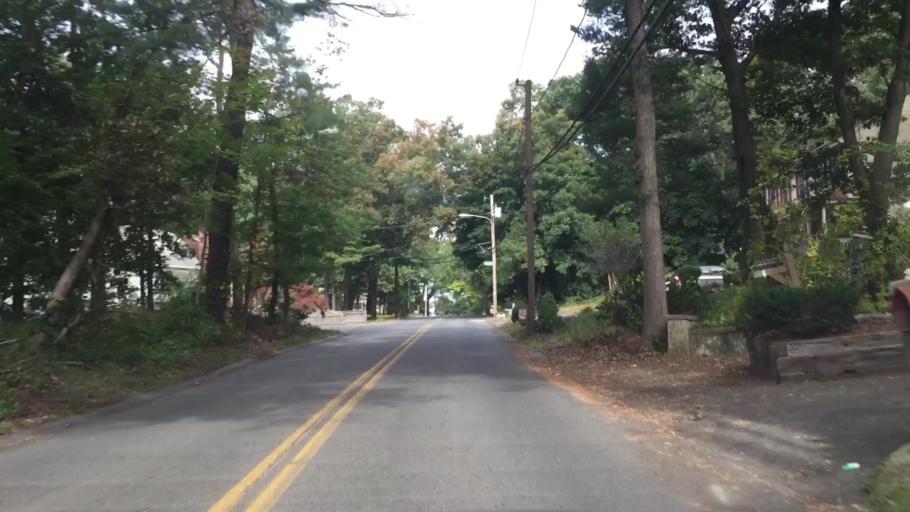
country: US
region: Massachusetts
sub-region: Middlesex County
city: Lowell
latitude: 42.6636
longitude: -71.3422
